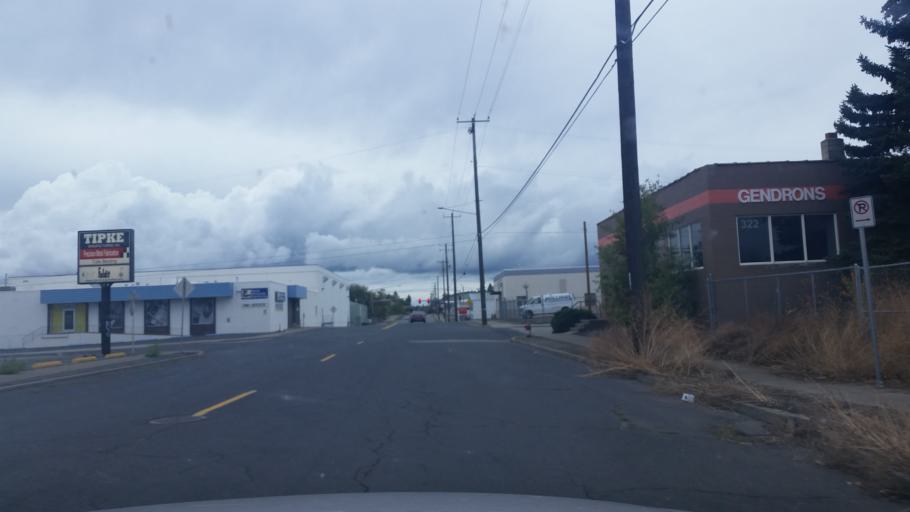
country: US
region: Washington
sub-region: Spokane County
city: Spokane
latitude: 47.6601
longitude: -117.3872
